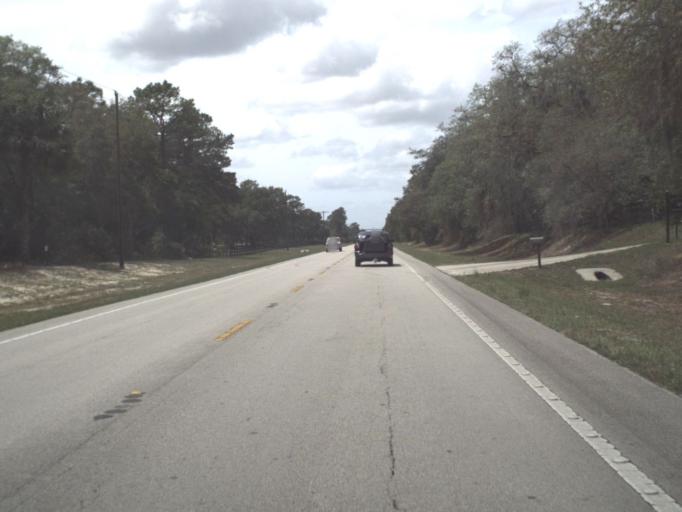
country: US
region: Florida
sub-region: Lake County
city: Mount Plymouth
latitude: 28.8677
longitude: -81.5008
